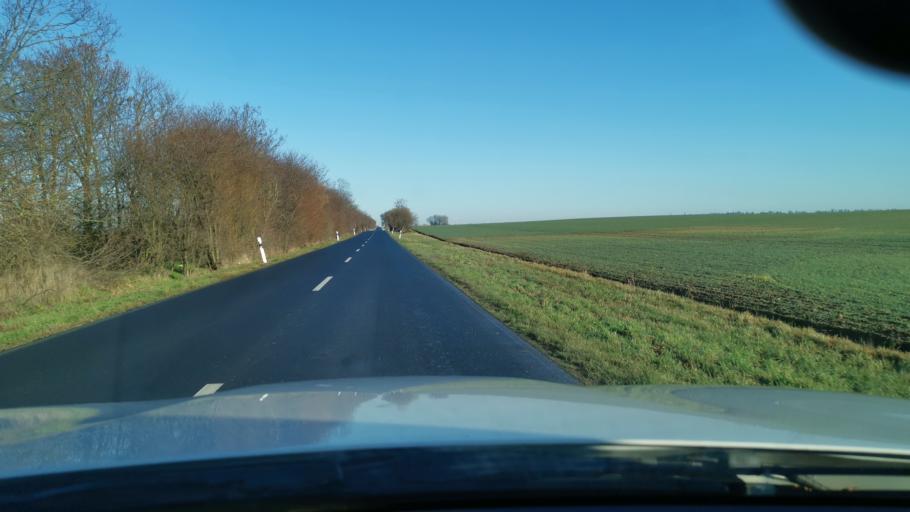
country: DE
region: Saxony-Anhalt
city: Seyda
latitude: 51.9630
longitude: 12.9000
